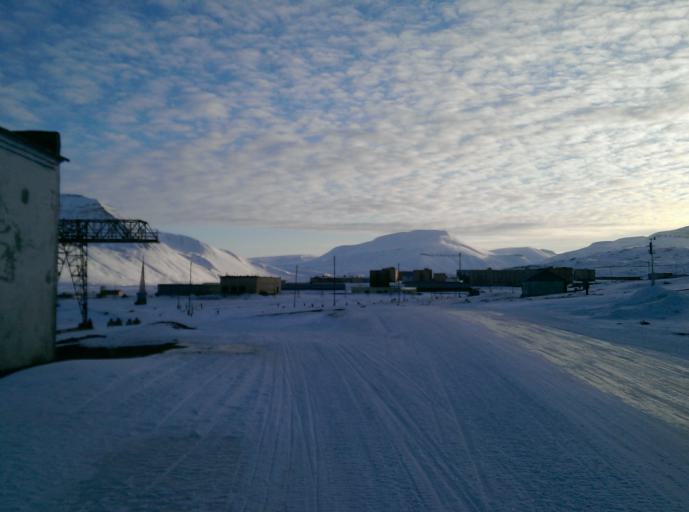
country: SJ
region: Svalbard
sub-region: Spitsbergen
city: Longyearbyen
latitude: 78.6555
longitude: 16.3587
